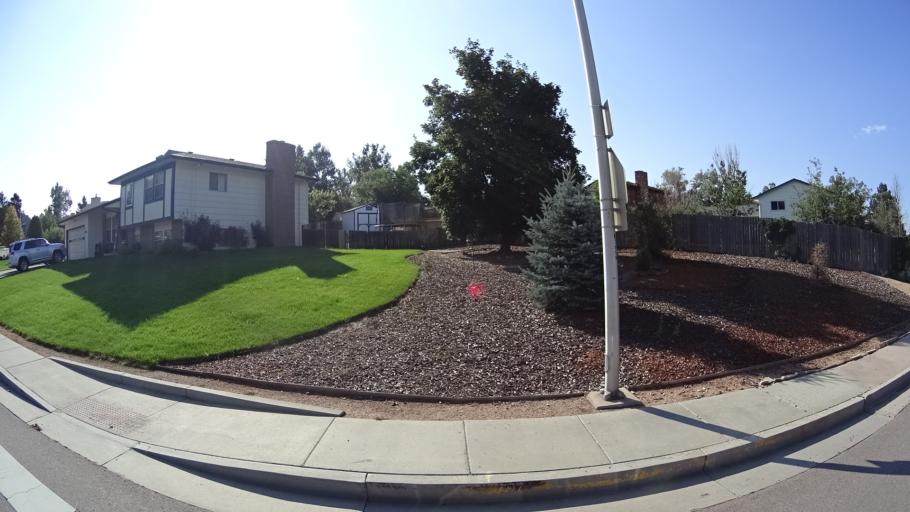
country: US
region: Colorado
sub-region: El Paso County
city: Air Force Academy
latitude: 38.9465
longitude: -104.7835
